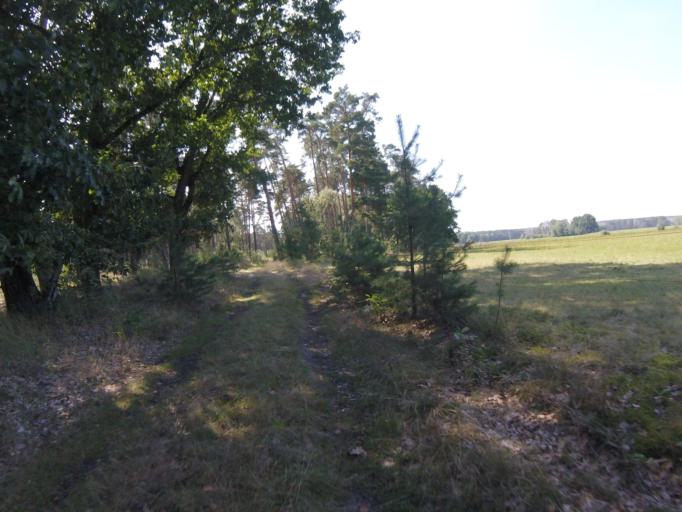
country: DE
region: Brandenburg
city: Bestensee
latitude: 52.2237
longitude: 13.6988
